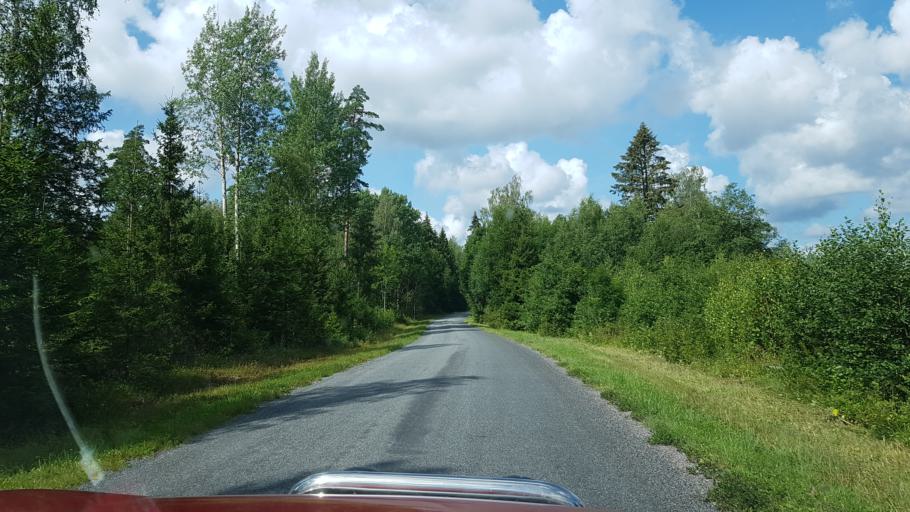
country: EE
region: Raplamaa
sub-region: Rapla vald
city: Rapla
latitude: 58.9532
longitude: 24.6667
